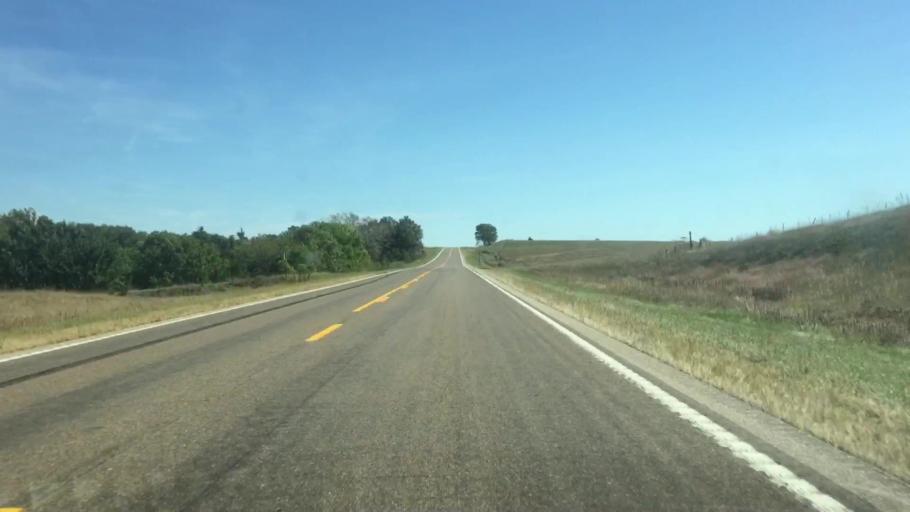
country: US
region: Nebraska
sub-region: Thayer County
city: Hebron
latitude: 40.1472
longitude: -97.5162
